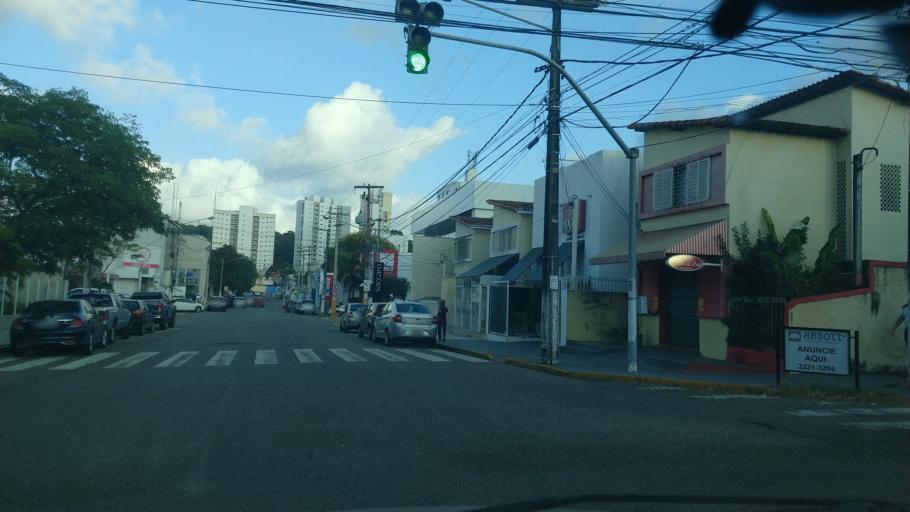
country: BR
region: Rio Grande do Norte
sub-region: Natal
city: Natal
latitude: -5.7882
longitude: -35.1987
